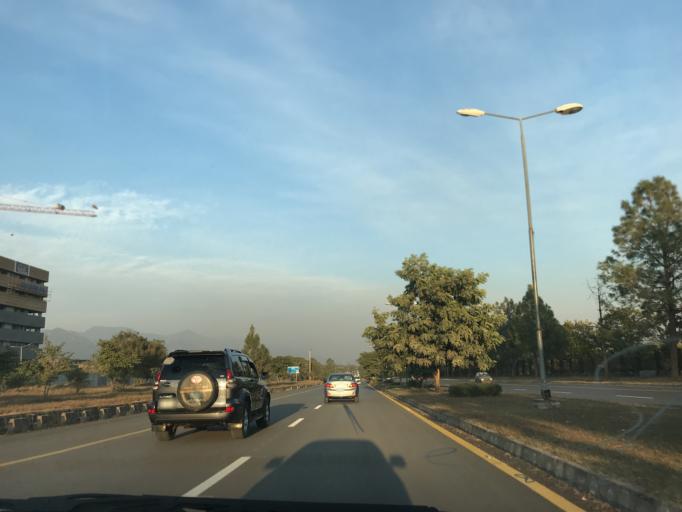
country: PK
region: Islamabad
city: Islamabad
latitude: 33.7069
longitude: 73.0148
